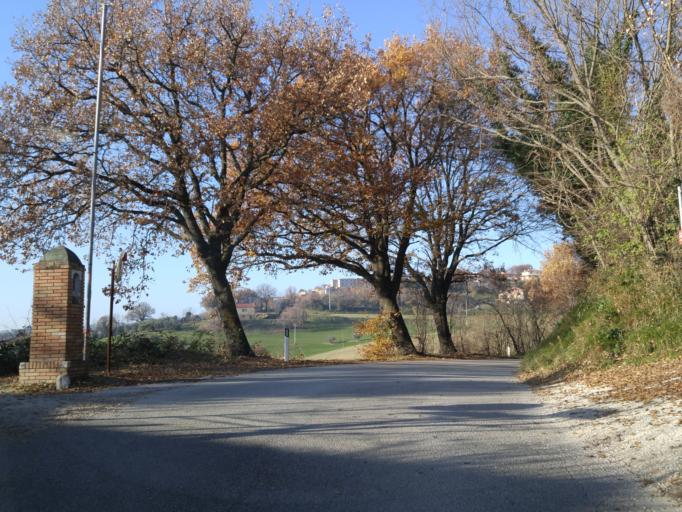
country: IT
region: The Marches
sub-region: Provincia di Pesaro e Urbino
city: Montefelcino
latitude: 43.7300
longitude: 12.8397
